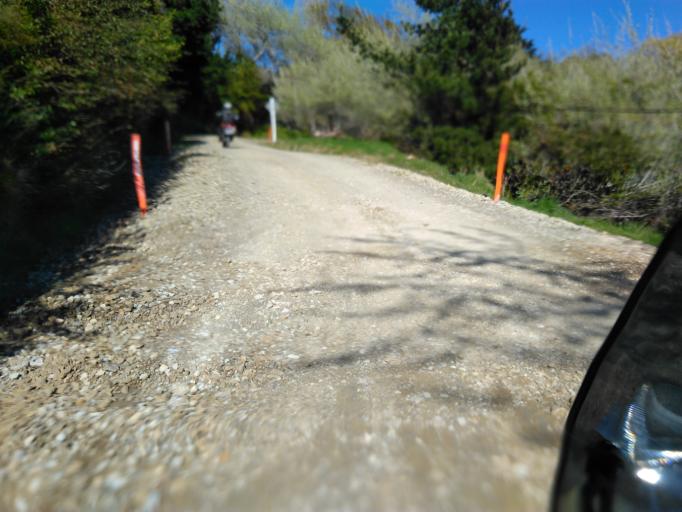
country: NZ
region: Bay of Plenty
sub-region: Opotiki District
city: Opotiki
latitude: -38.3707
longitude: 177.6020
